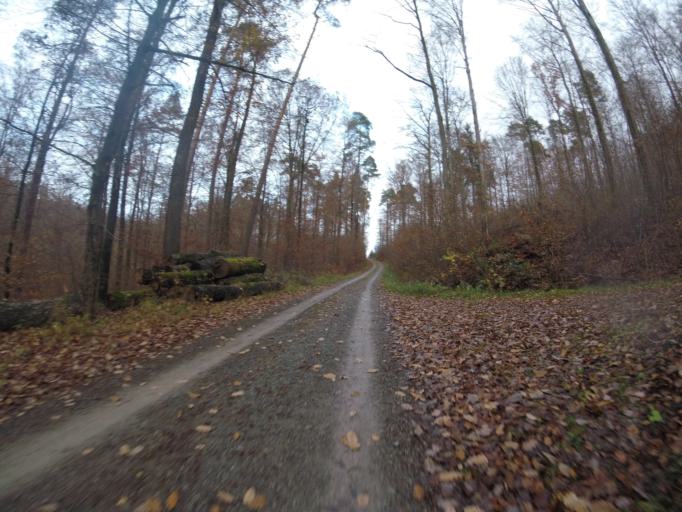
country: DE
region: Baden-Wuerttemberg
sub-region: Regierungsbezirk Stuttgart
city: Aspach
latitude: 49.0045
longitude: 9.3969
